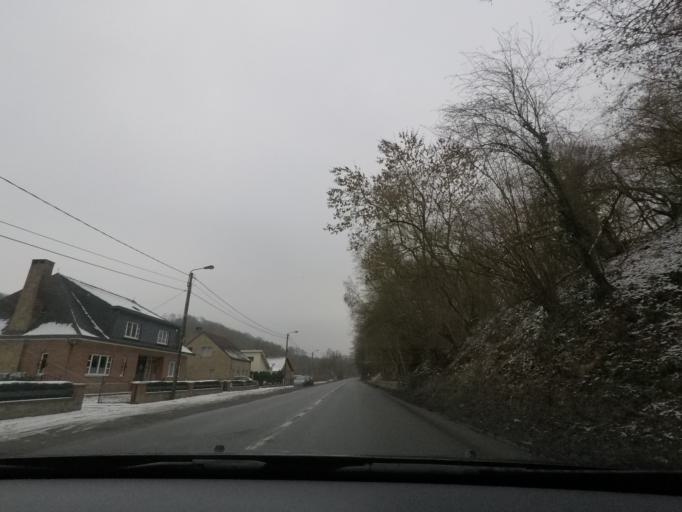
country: BE
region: Wallonia
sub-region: Province de Namur
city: Sombreffe
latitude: 50.4813
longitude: 4.6692
